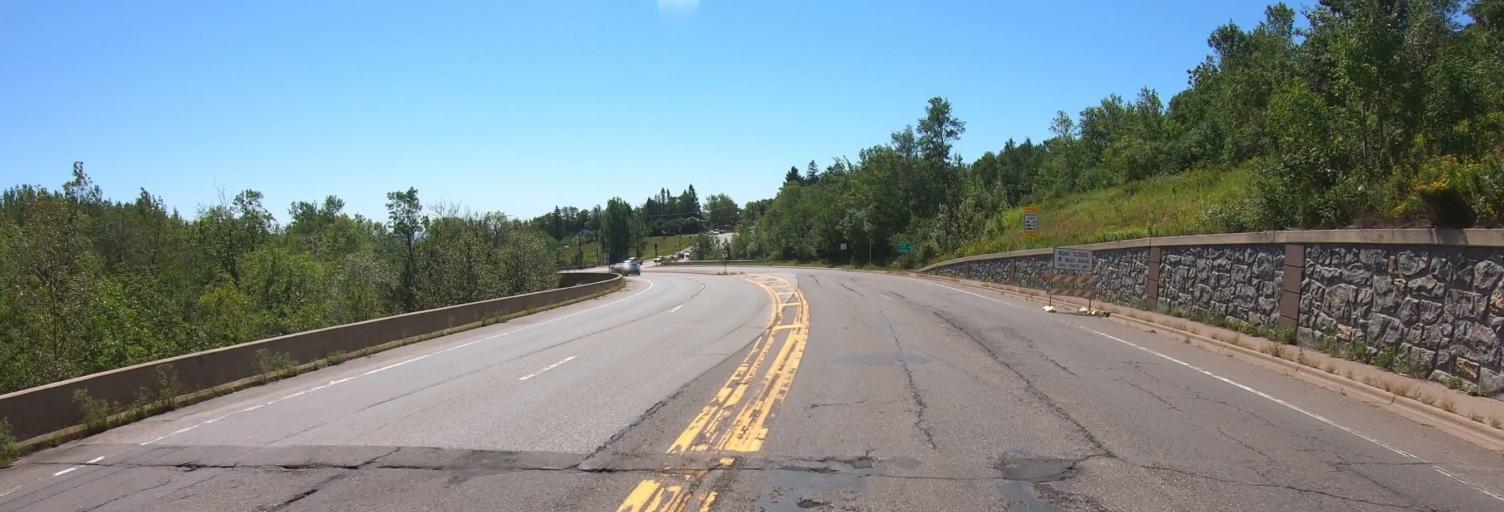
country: US
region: Minnesota
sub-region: Saint Louis County
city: Duluth
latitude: 46.7767
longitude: -92.1425
